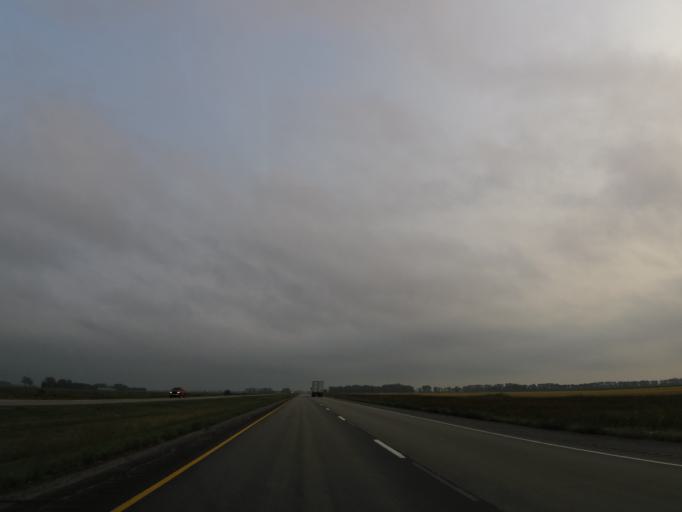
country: US
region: North Dakota
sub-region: Walsh County
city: Grafton
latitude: 48.5509
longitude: -97.1862
